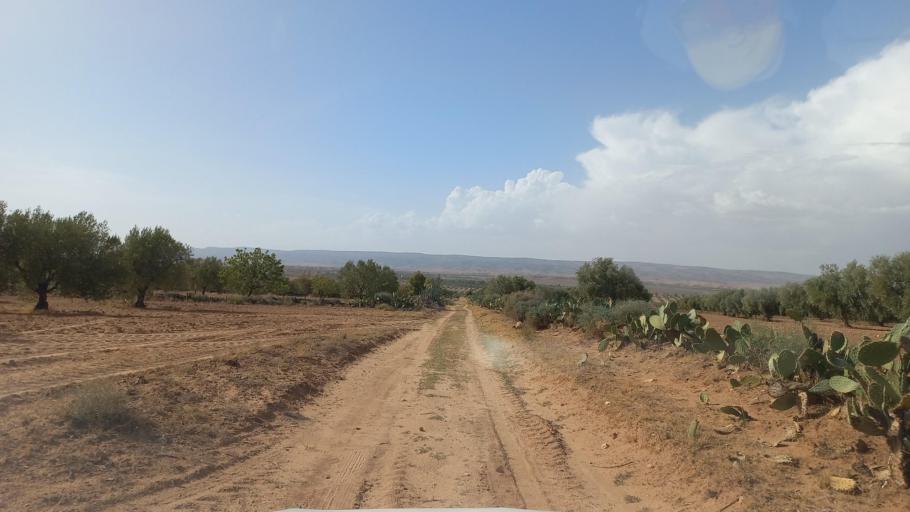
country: TN
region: Al Qasrayn
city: Kasserine
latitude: 35.2098
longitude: 8.9554
